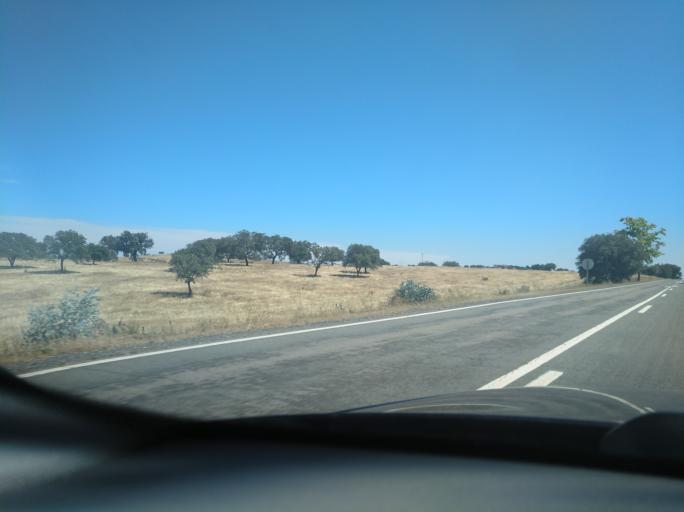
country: PT
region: Beja
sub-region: Castro Verde
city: Castro Verde
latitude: 37.6254
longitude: -8.0822
